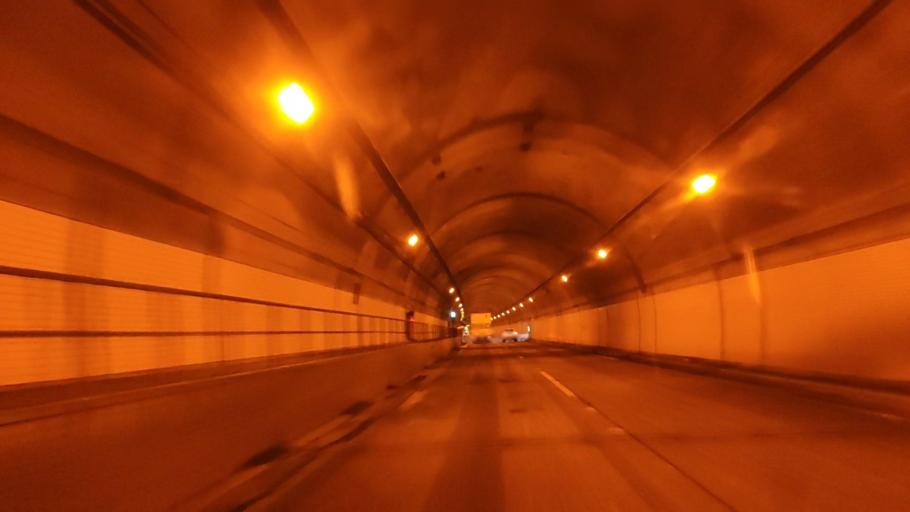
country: JP
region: Niigata
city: Itoigawa
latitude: 37.0558
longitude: 137.9268
